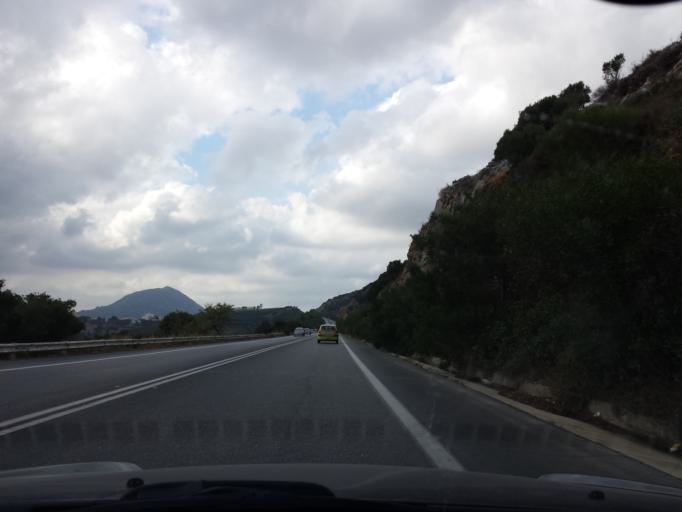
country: GR
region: Crete
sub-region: Nomos Lasithiou
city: Neapoli
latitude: 35.2519
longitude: 25.6220
